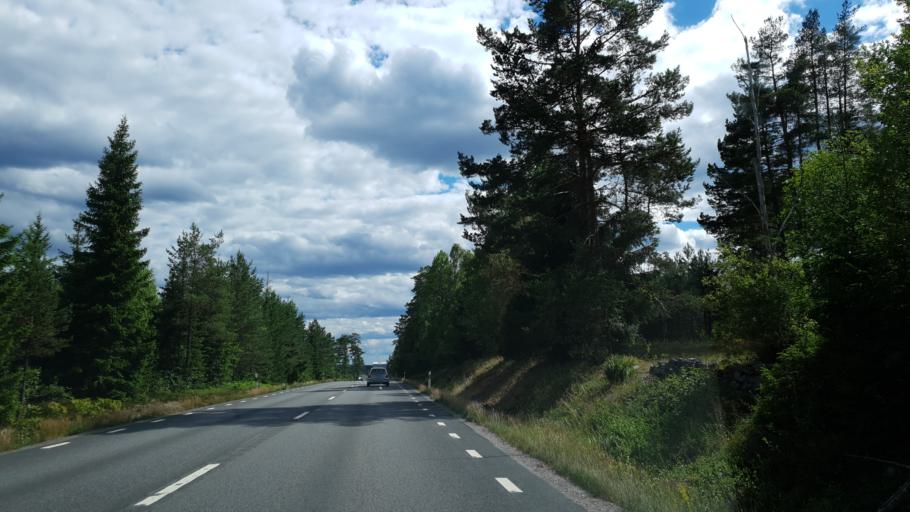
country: SE
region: Kronoberg
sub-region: Lessebo Kommun
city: Lessebo
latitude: 56.8134
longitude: 15.4114
